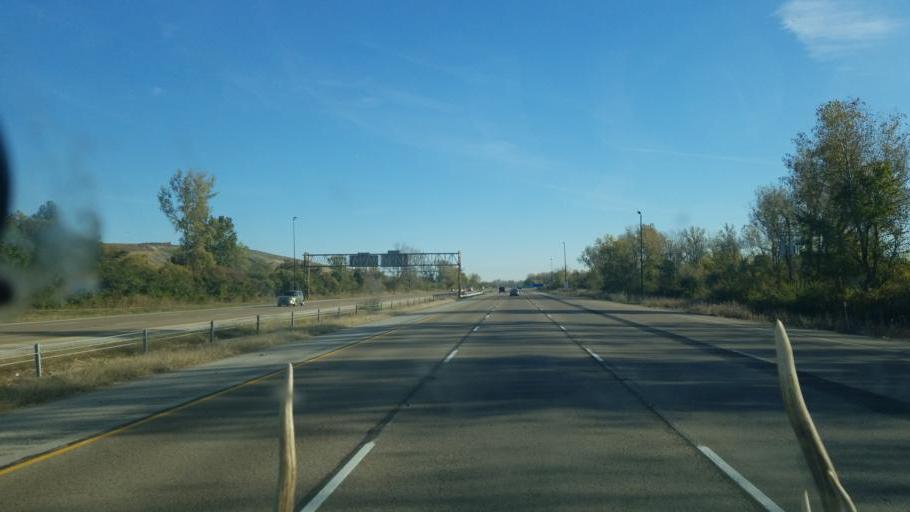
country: US
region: Illinois
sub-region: Saint Clair County
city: Fairmont City
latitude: 38.6468
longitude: -90.1260
